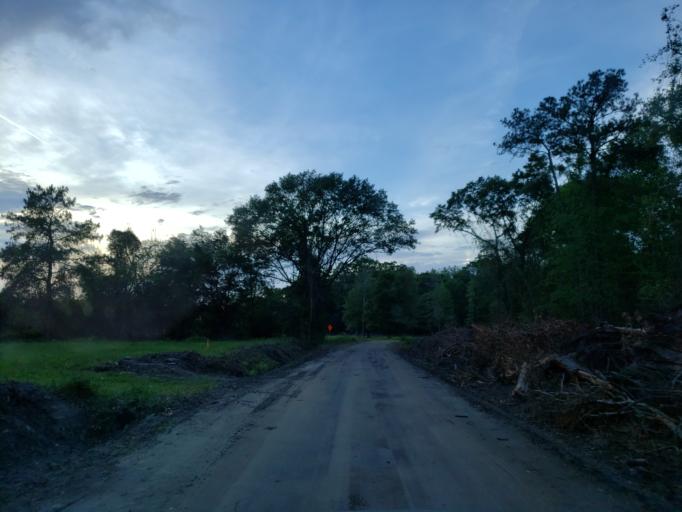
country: US
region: Georgia
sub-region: Lowndes County
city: Hahira
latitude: 30.9556
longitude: -83.3929
